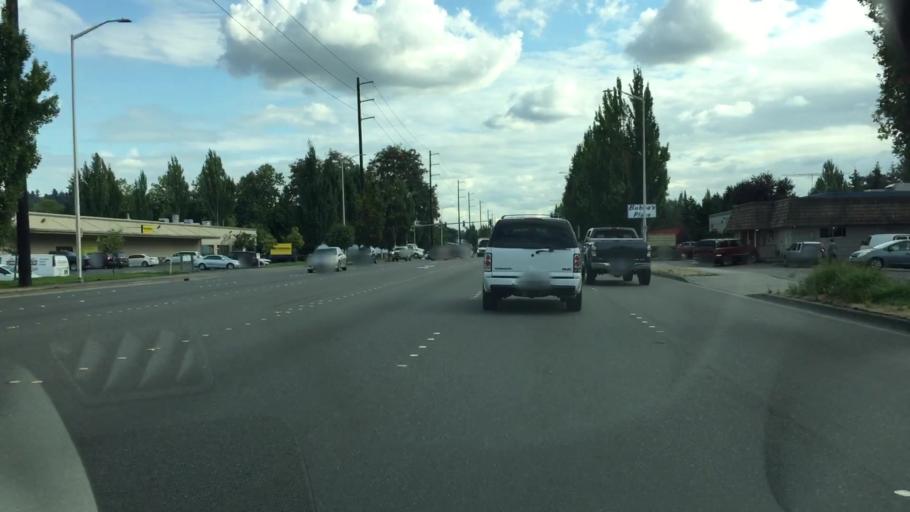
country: US
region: Washington
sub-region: King County
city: Kent
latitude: 47.4101
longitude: -122.2281
